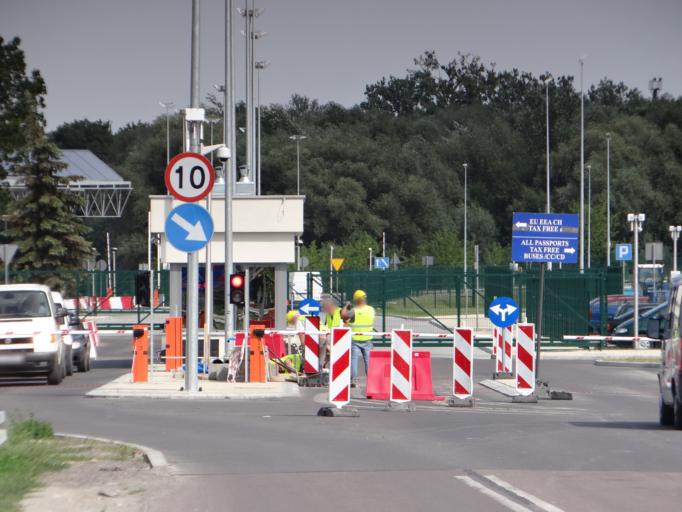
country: PL
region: Lublin Voivodeship
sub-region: Powiat hrubieszowski
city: Horodlo
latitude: 50.8598
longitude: 24.1318
